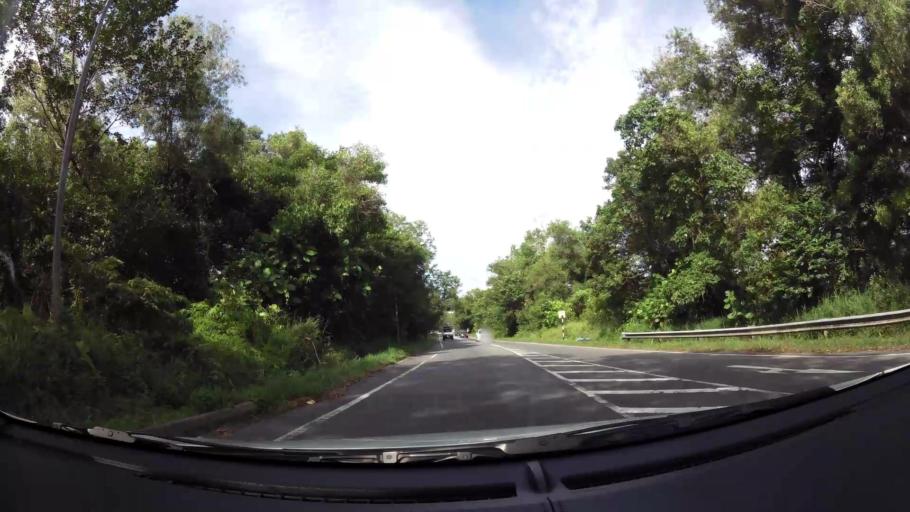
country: BN
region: Brunei and Muara
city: Bandar Seri Begawan
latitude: 4.9006
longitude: 114.8824
